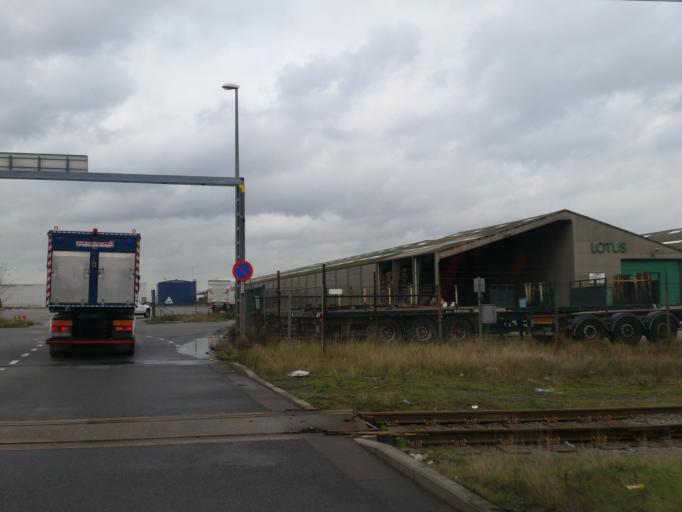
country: BE
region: Flanders
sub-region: Provincie Antwerpen
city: Stabroek
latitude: 51.2882
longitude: 4.3520
